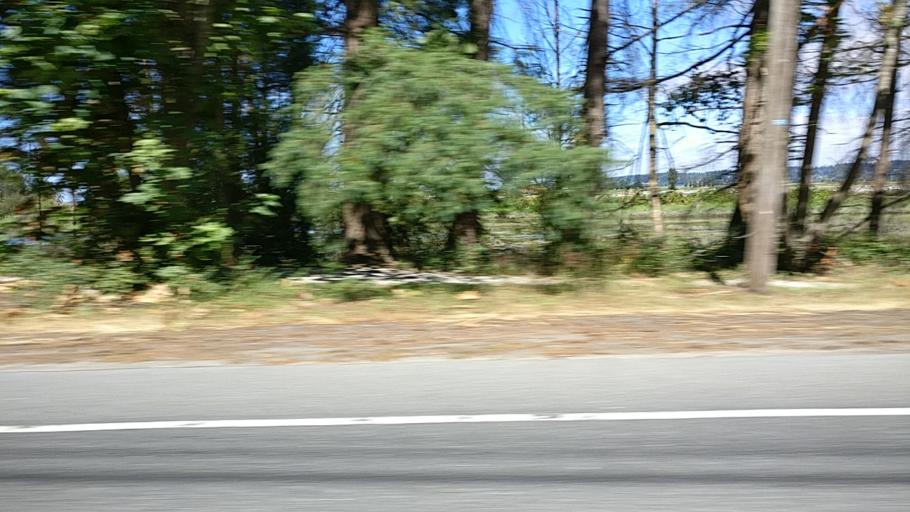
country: CA
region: British Columbia
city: Surrey
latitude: 49.0658
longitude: -122.8380
